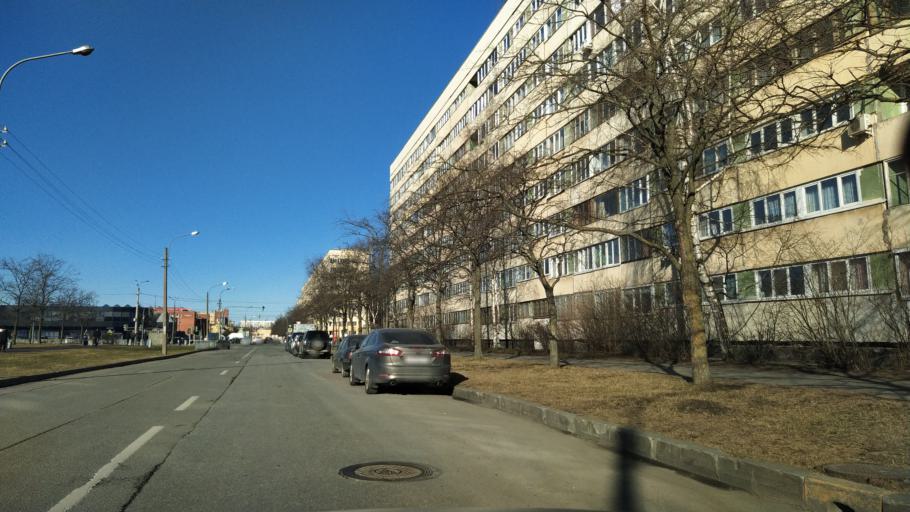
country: RU
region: St.-Petersburg
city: Grazhdanka
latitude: 60.0399
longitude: 30.3909
